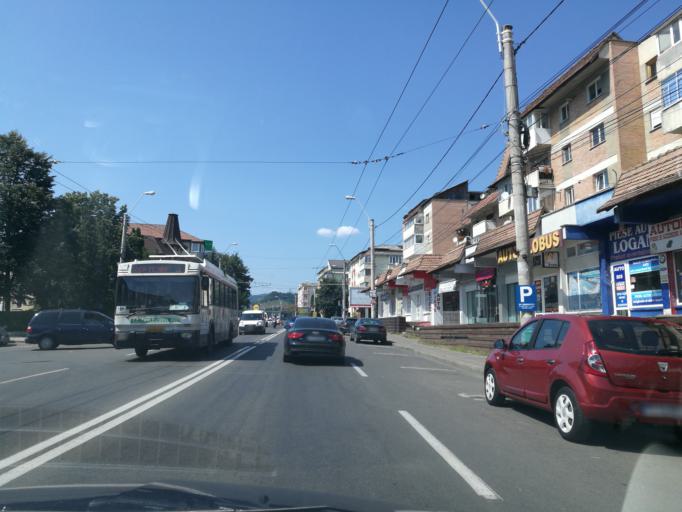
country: RO
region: Neamt
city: Piatra Neamt
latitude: 46.9361
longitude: 26.3512
